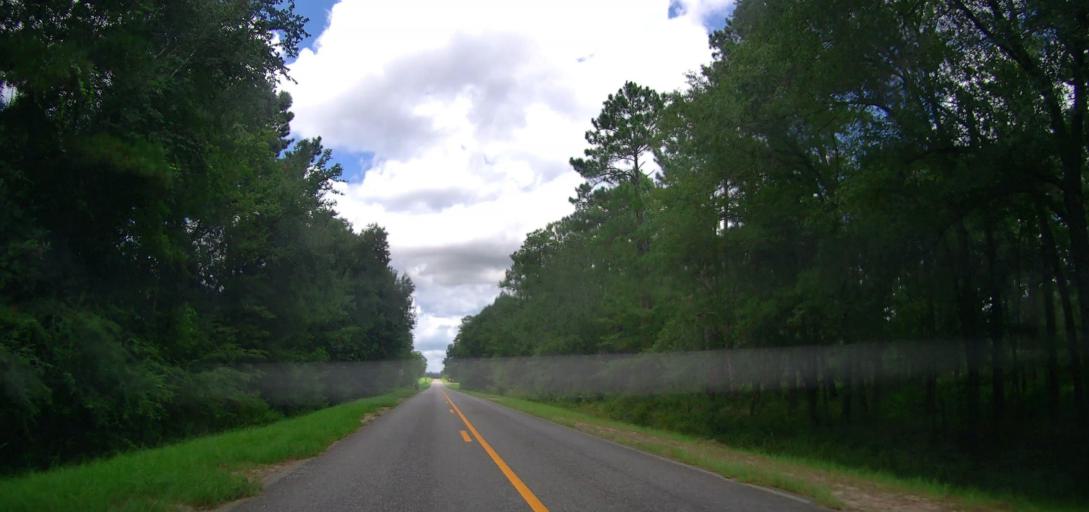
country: US
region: Georgia
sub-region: Turner County
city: Ashburn
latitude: 31.7184
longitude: -83.5056
